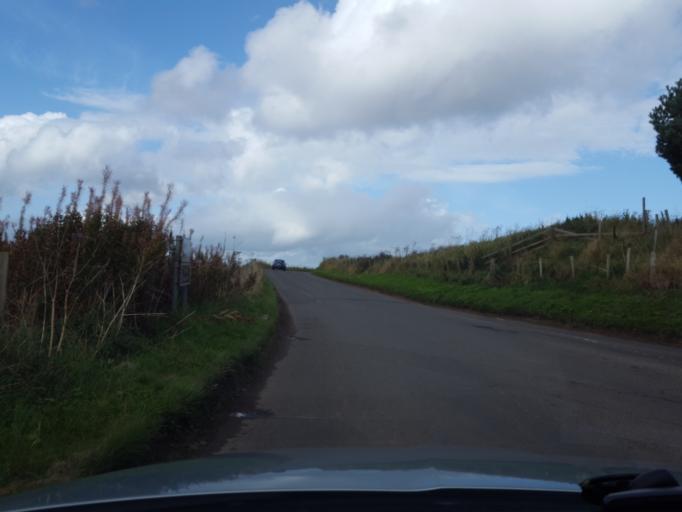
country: GB
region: Scotland
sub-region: Fife
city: Newport-On-Tay
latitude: 56.4145
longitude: -2.9719
